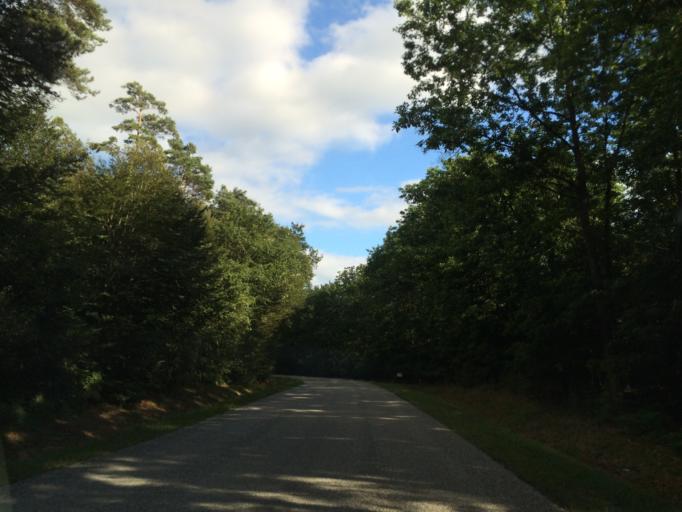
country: FR
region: Alsace
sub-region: Departement du Bas-Rhin
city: Soufflenheim
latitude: 48.8504
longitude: 7.9473
